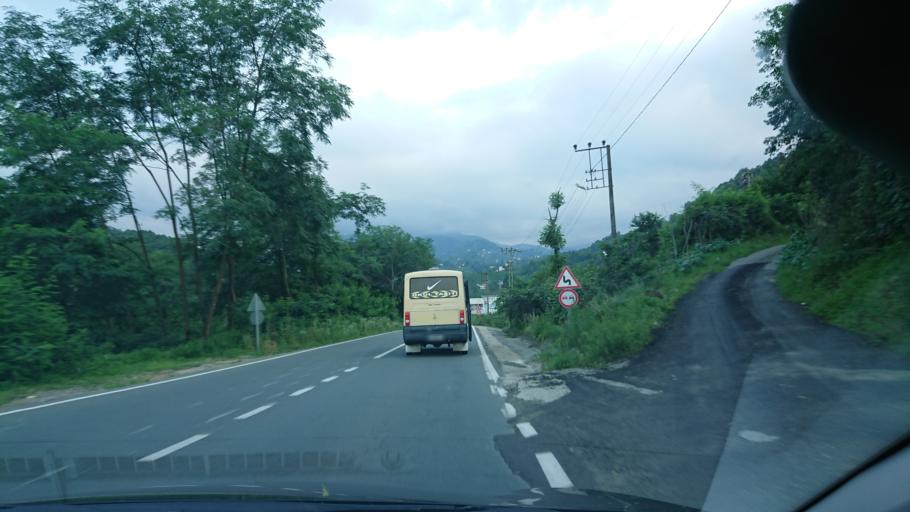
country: TR
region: Rize
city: Cayeli
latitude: 41.0659
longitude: 40.7148
